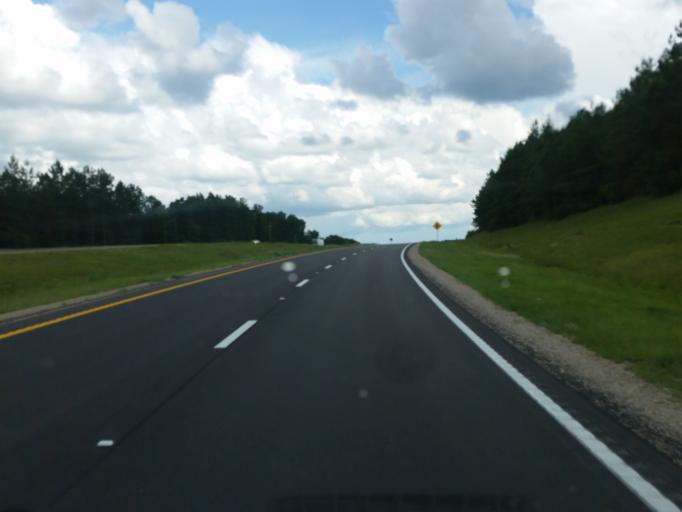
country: US
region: Mississippi
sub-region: Greene County
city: Leakesville
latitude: 31.0716
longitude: -88.7415
